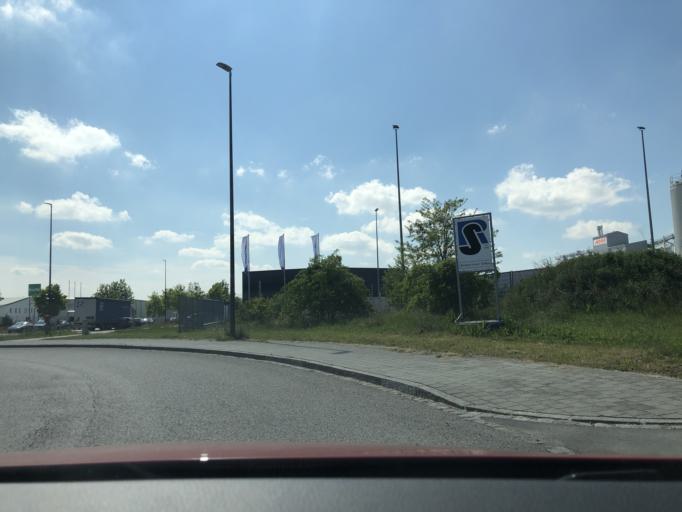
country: DE
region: Bavaria
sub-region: Upper Bavaria
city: Grossmehring
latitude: 48.7890
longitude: 11.5115
